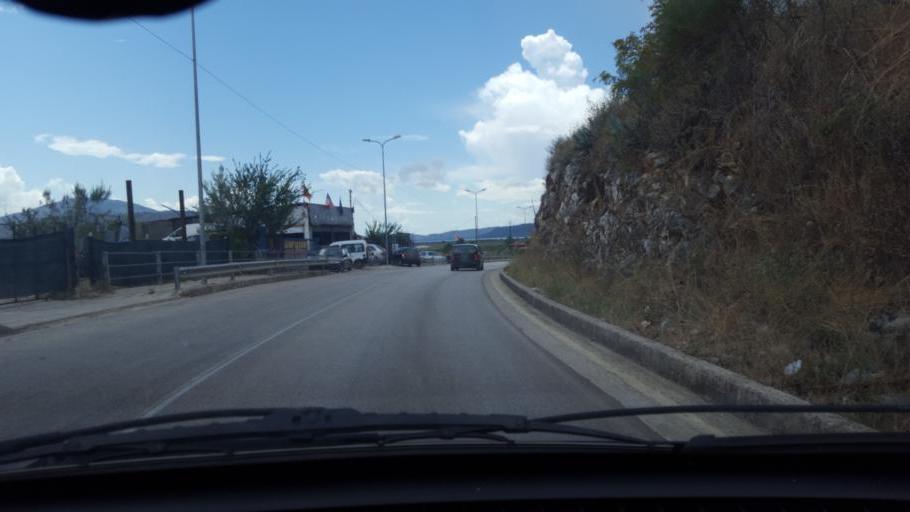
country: AL
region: Vlore
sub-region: Rrethi i Sarandes
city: Sarande
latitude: 39.8421
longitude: 20.0252
